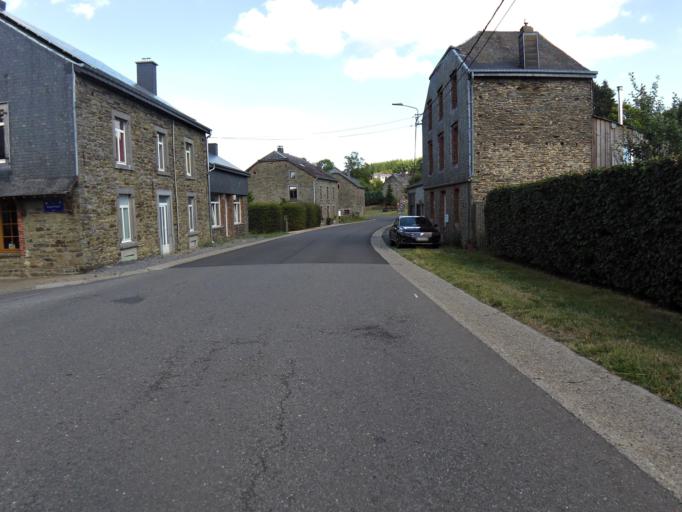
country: BE
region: Wallonia
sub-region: Province de Namur
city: Bievre
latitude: 49.8936
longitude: 5.0090
